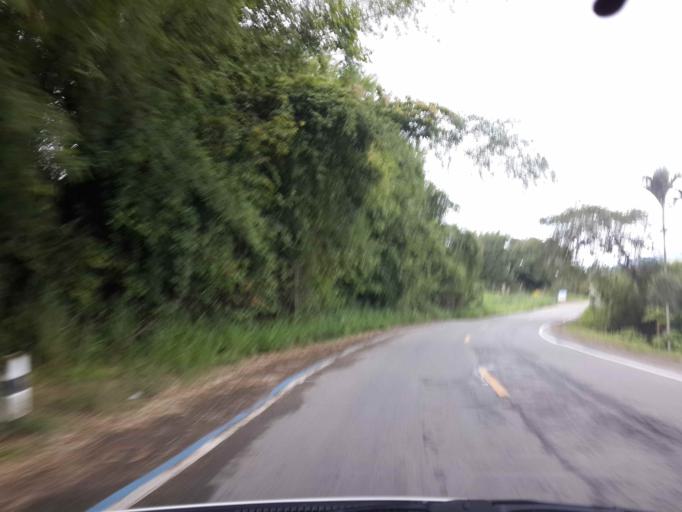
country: TH
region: Ratchaburi
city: Suan Phueng
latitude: 13.6336
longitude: 99.2186
